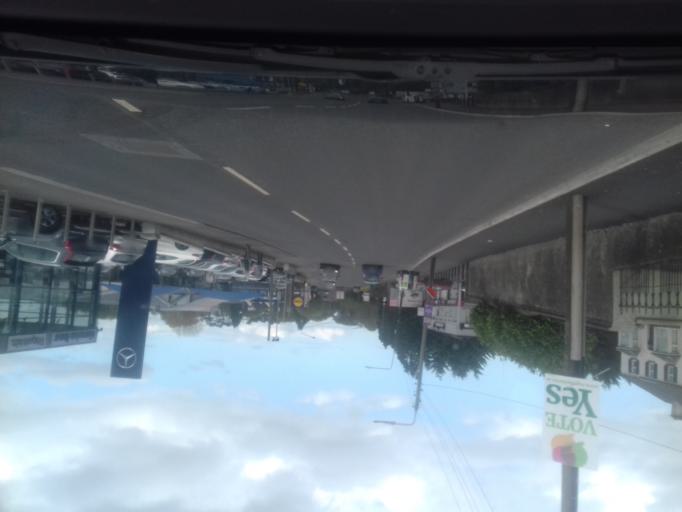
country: IE
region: Leinster
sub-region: Kildare
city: Kildare
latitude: 53.1556
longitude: -6.9062
